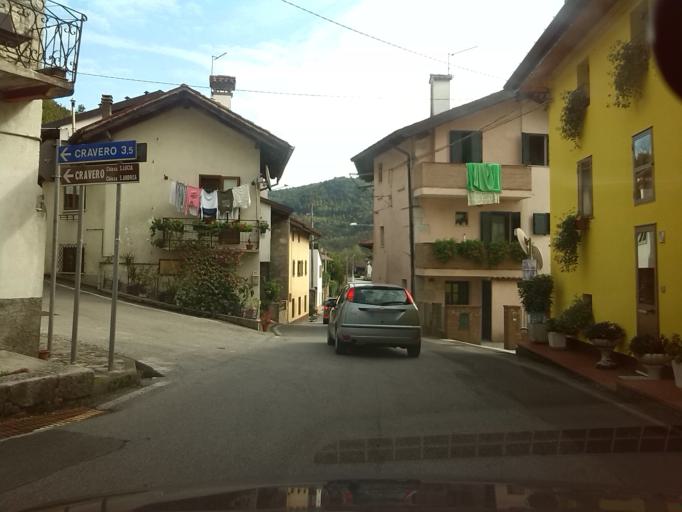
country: IT
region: Friuli Venezia Giulia
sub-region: Provincia di Udine
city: Merso di Sopra
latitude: 46.1218
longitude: 13.5281
